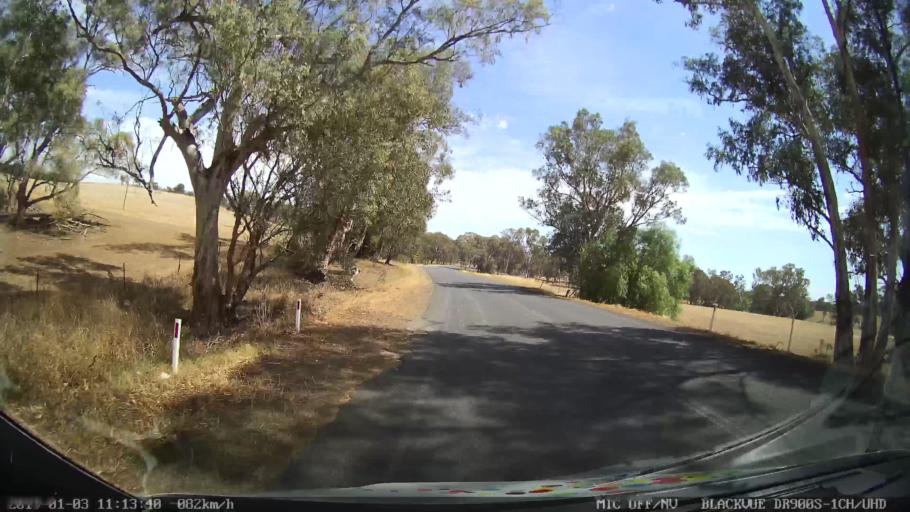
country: AU
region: New South Wales
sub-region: Young
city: Young
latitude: -34.1857
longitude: 148.2606
